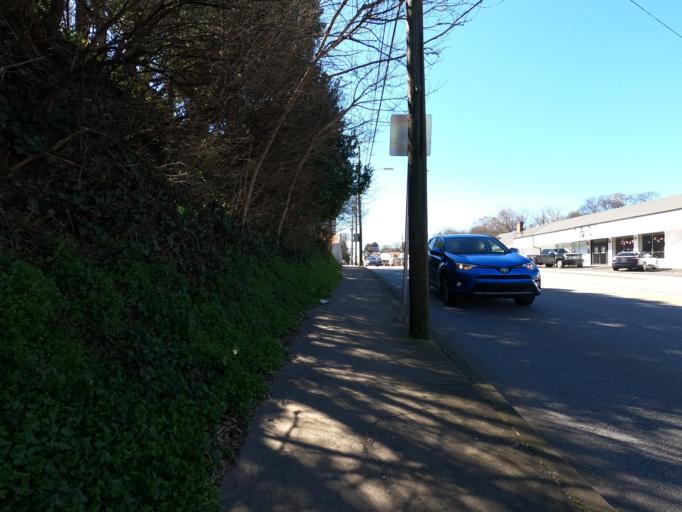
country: US
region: Georgia
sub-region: Clarke County
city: Athens
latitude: 33.9561
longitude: -83.3832
